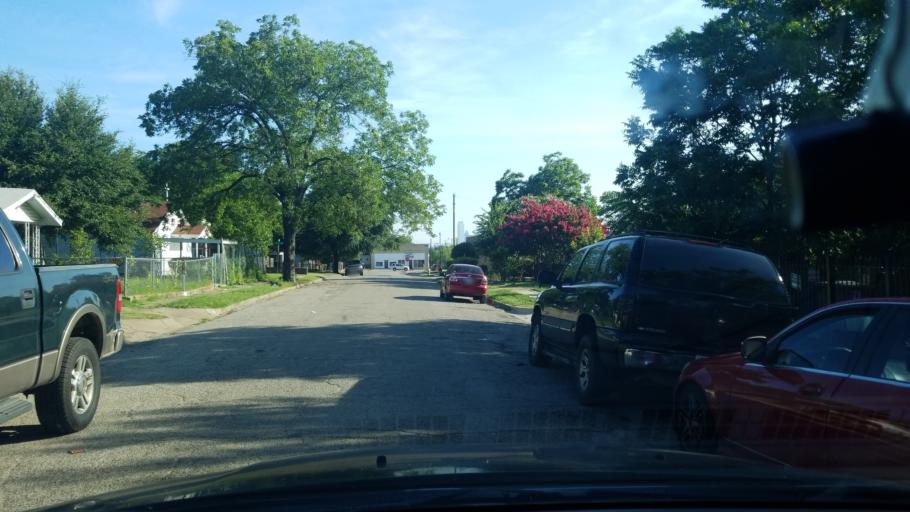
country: US
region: Texas
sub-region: Dallas County
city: Dallas
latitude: 32.7256
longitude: -96.8120
